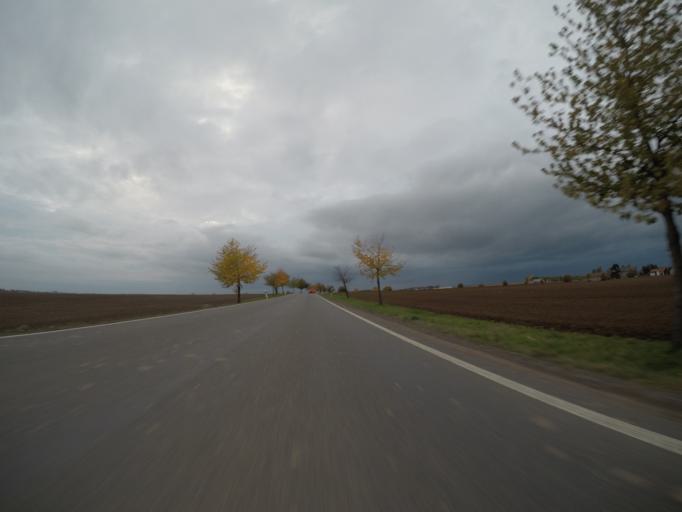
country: DE
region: Thuringia
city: Nobitz
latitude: 50.9336
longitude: 12.5016
